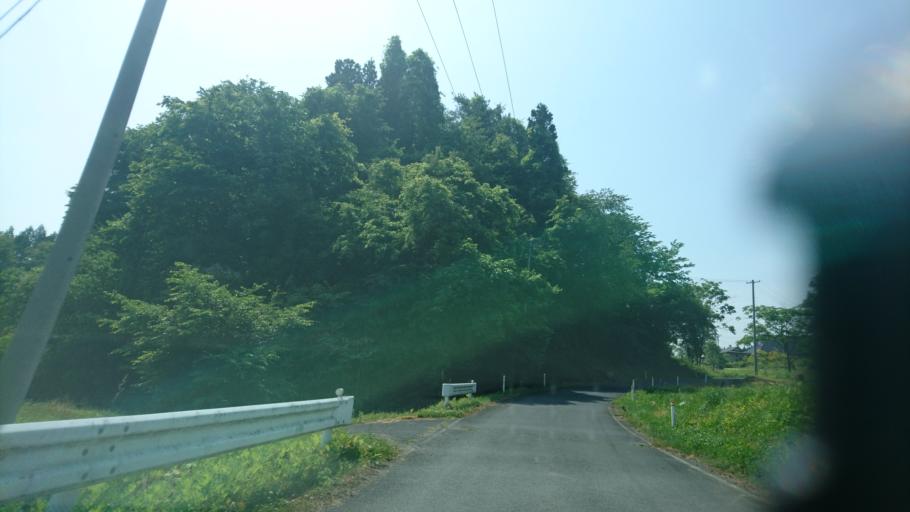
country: JP
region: Iwate
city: Ichinoseki
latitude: 38.8955
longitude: 141.3364
